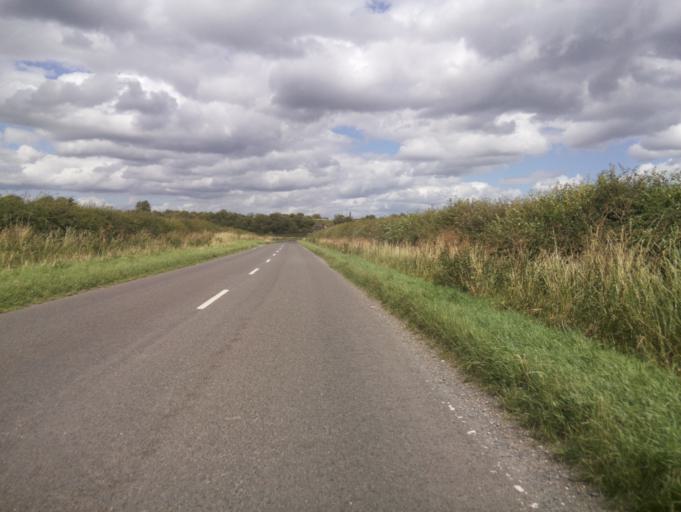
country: GB
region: England
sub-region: Nottinghamshire
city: West Bridgford
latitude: 52.8866
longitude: -1.0964
